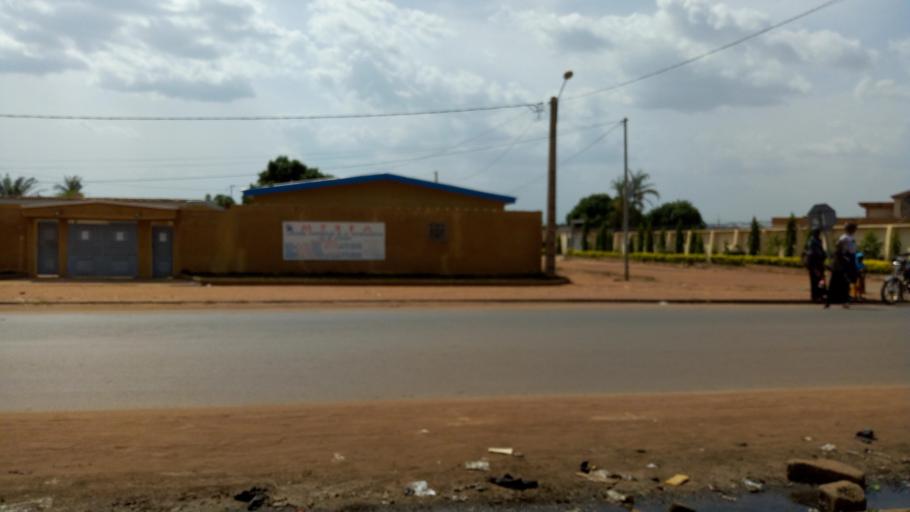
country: CI
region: Vallee du Bandama
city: Bouake
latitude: 7.7100
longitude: -5.0460
